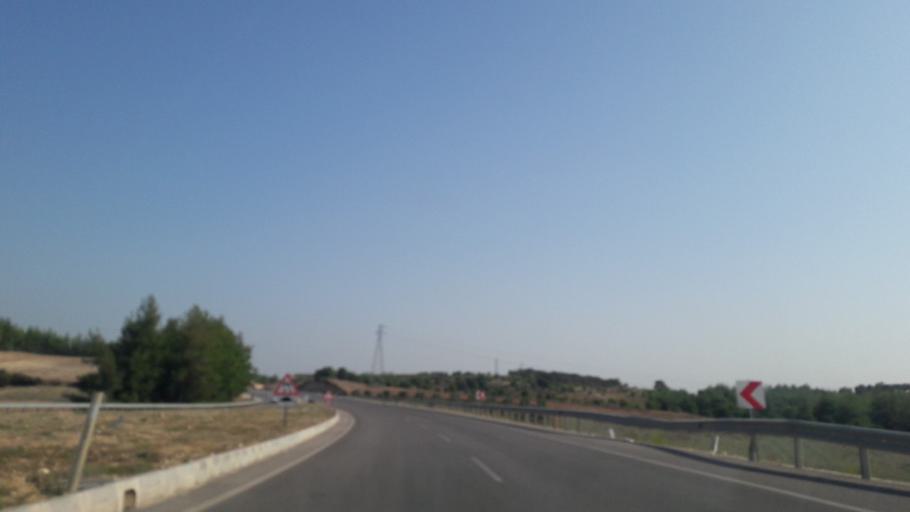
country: TR
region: Adana
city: Sagkaya
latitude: 37.1607
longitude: 35.5551
